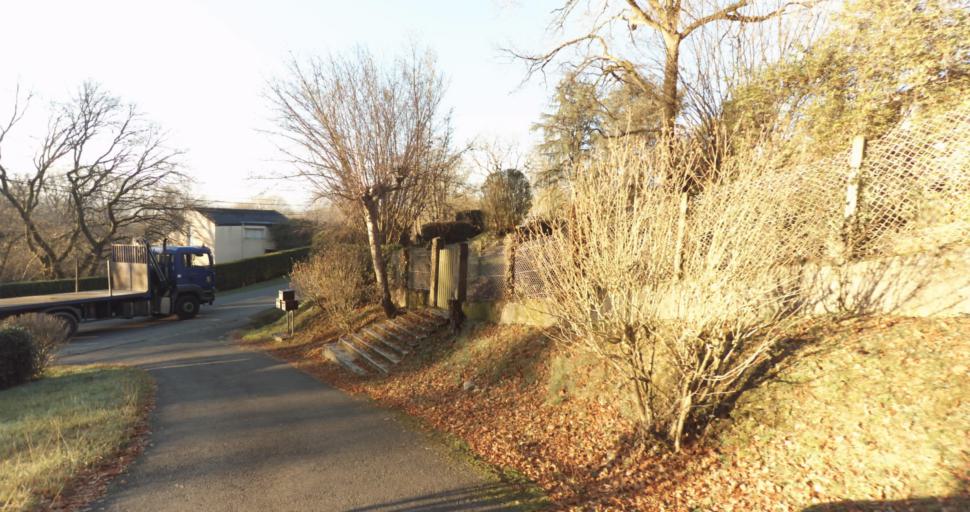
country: FR
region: Aquitaine
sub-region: Departement des Pyrenees-Atlantiques
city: Morlaas
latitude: 43.3305
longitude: -0.2718
